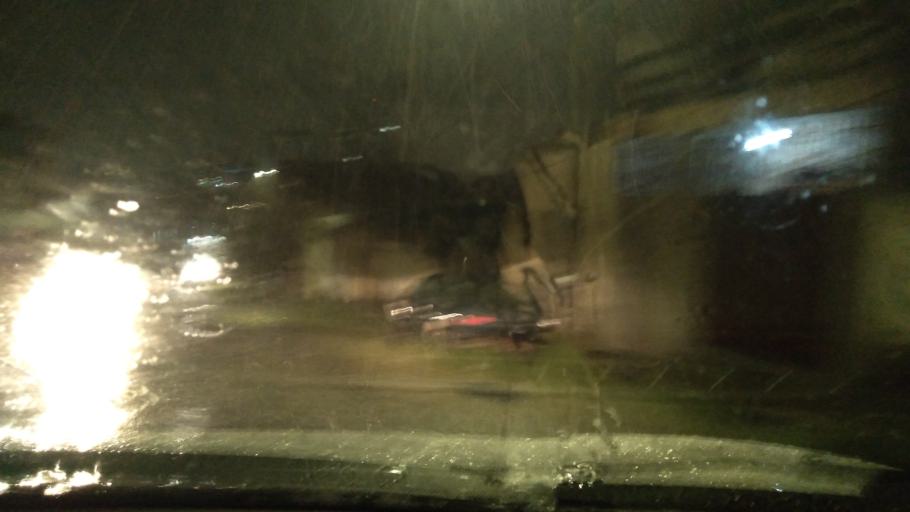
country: BR
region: Minas Gerais
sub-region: Belo Horizonte
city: Belo Horizonte
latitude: -19.8812
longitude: -43.9417
